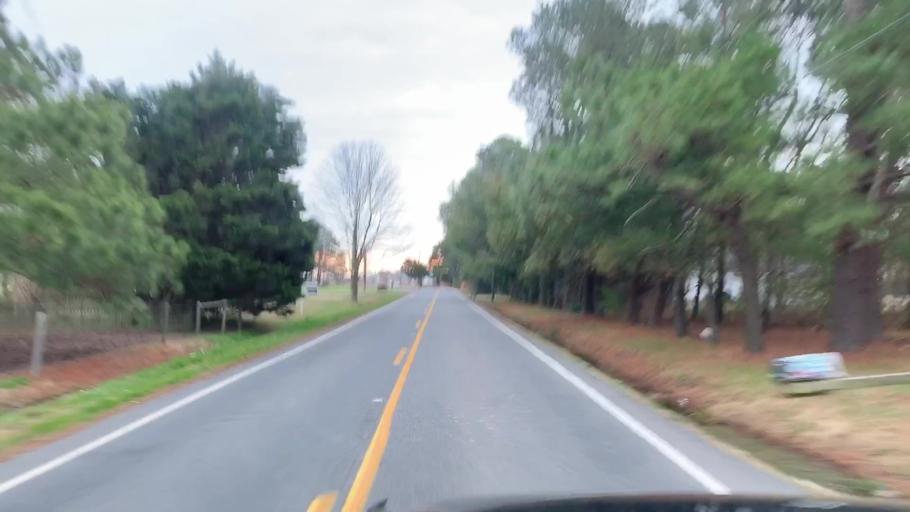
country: US
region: North Carolina
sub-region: Currituck County
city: Moyock
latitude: 36.6247
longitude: -76.1606
